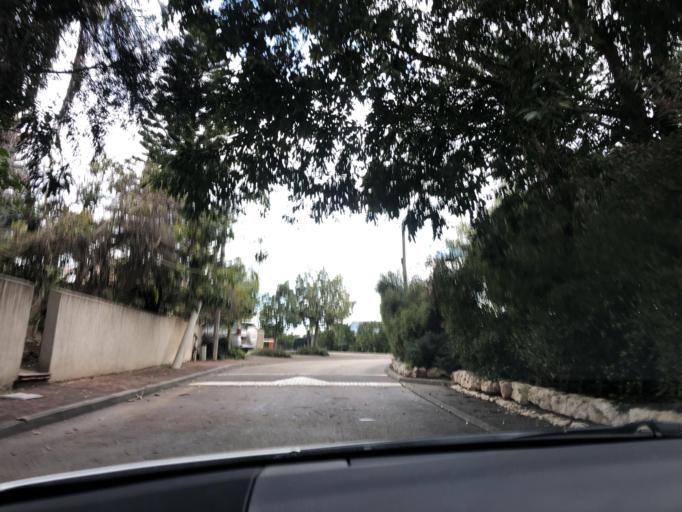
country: IL
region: Central District
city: Tel Mond
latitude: 32.2648
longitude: 34.9299
